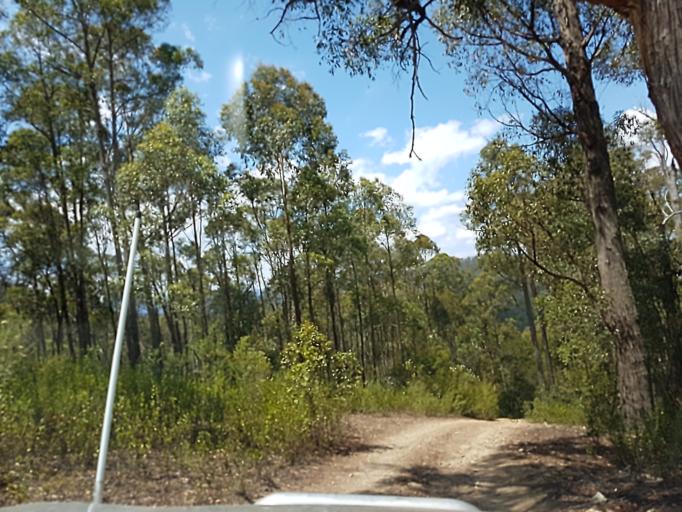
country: AU
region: Victoria
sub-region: East Gippsland
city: Lakes Entrance
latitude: -37.4070
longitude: 148.3043
